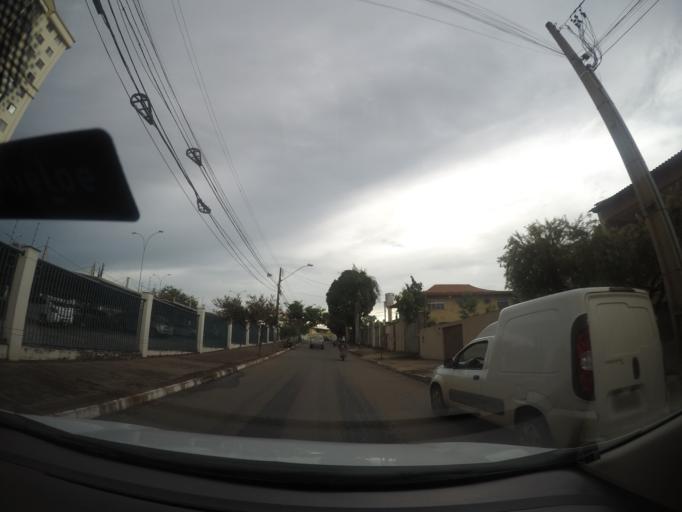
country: BR
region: Goias
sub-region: Goiania
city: Goiania
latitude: -16.6889
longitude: -49.3017
